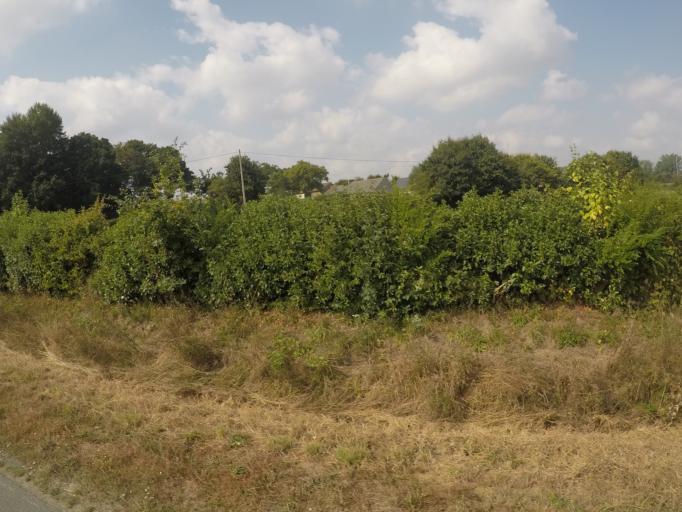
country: FR
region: Brittany
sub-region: Departement des Cotes-d'Armor
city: Saint-Donan
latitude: 48.5138
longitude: -2.9108
